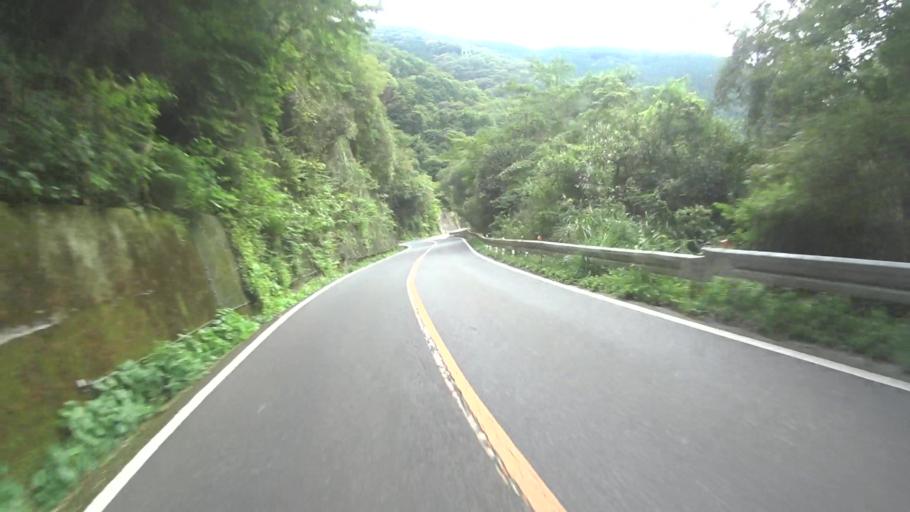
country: JP
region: Kyoto
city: Uji
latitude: 34.8943
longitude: 135.8685
